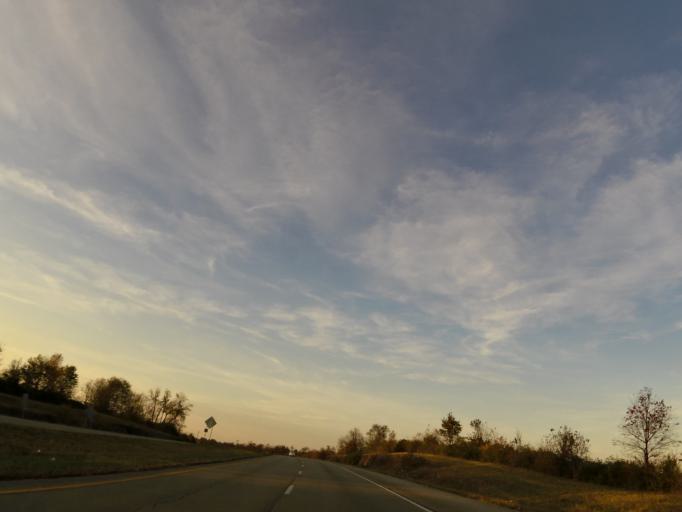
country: US
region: Kentucky
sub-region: Jessamine County
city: Nicholasville
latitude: 37.8534
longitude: -84.5874
